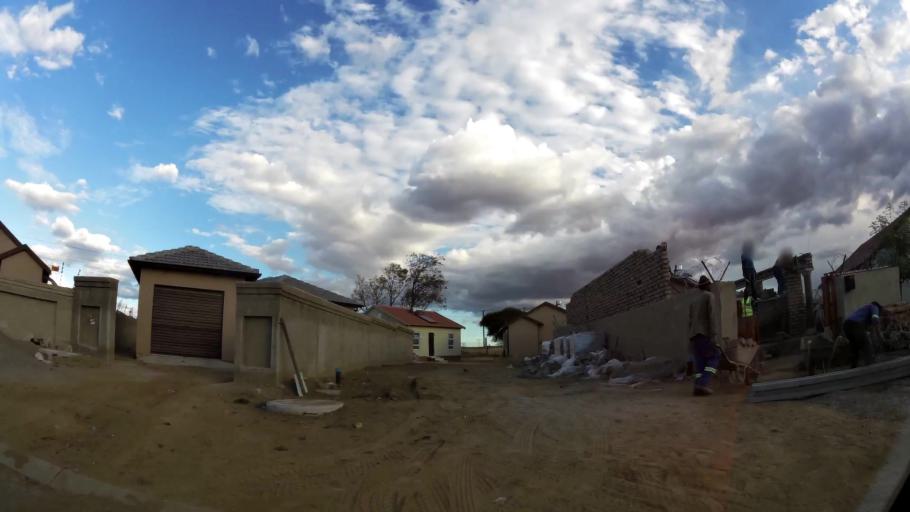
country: ZA
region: Limpopo
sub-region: Capricorn District Municipality
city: Polokwane
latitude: -23.9303
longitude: 29.4142
